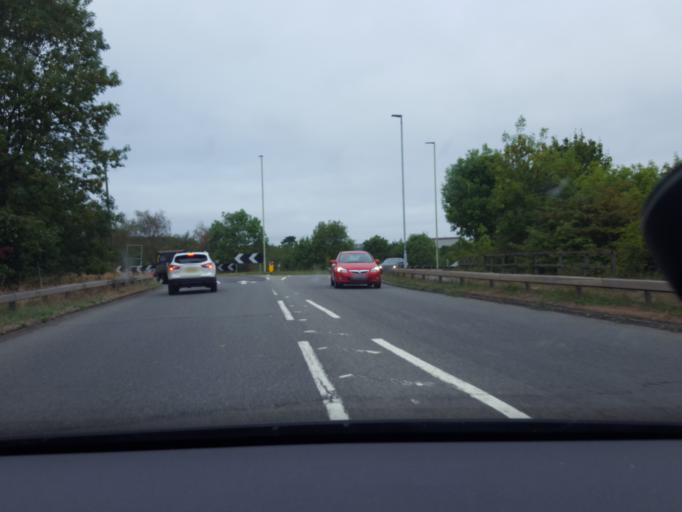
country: GB
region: England
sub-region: Leicestershire
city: Shepshed
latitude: 52.7604
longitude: -1.2714
